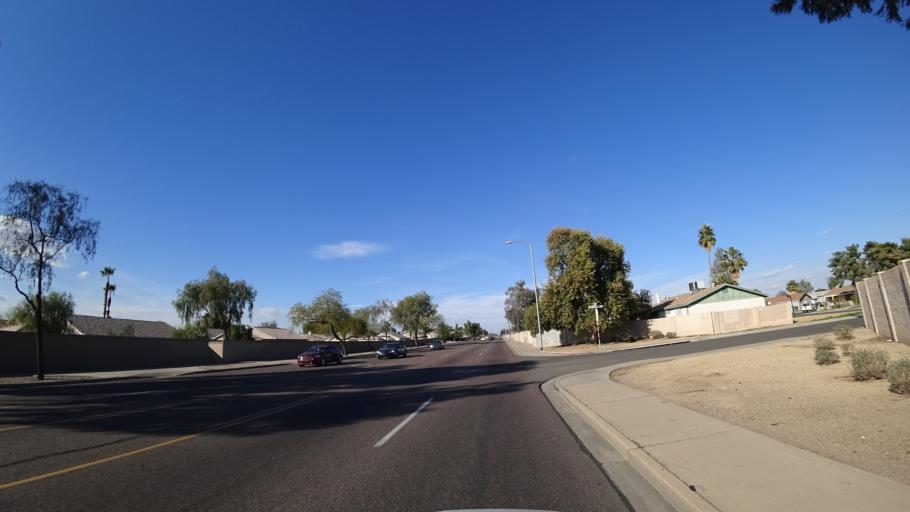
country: US
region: Arizona
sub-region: Maricopa County
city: Tolleson
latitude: 33.5024
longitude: -112.2377
